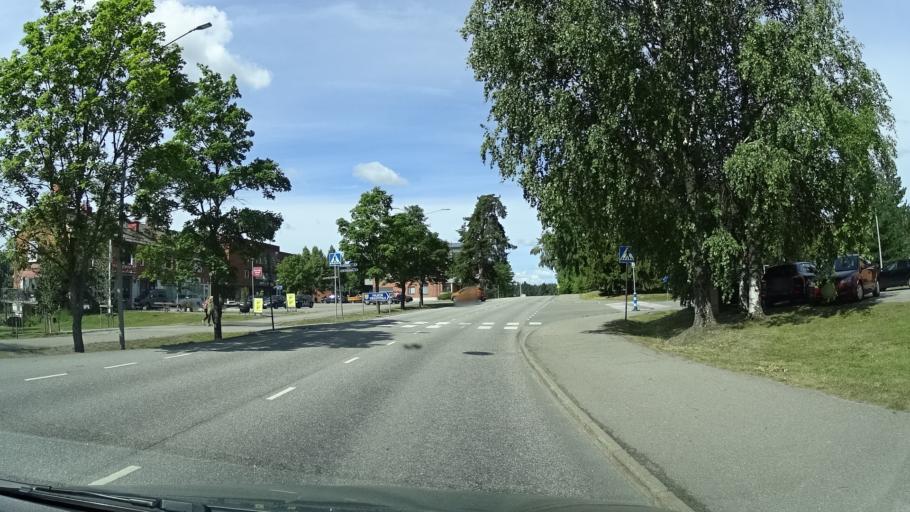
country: FI
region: Varsinais-Suomi
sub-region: Salo
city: Halikko
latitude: 60.3971
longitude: 23.0756
